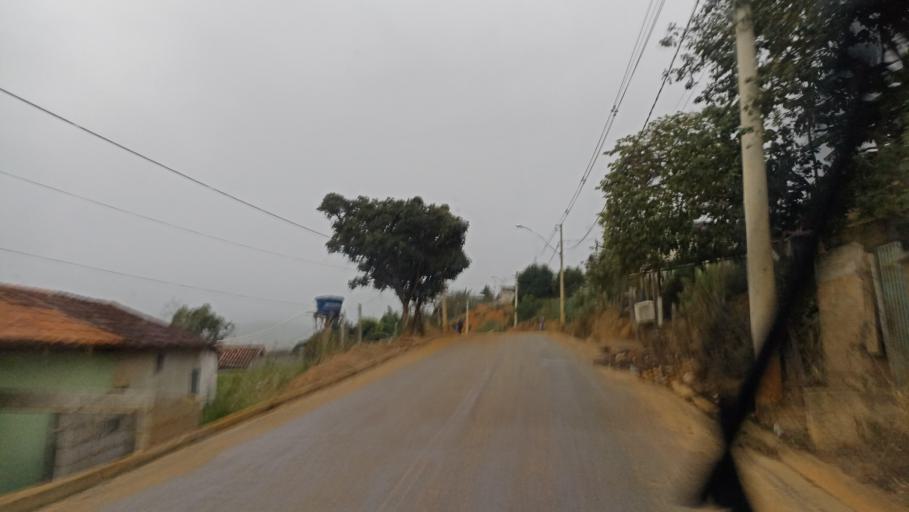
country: BR
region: Bahia
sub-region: Itanhem
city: Itanhem
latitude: -16.7347
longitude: -40.4287
